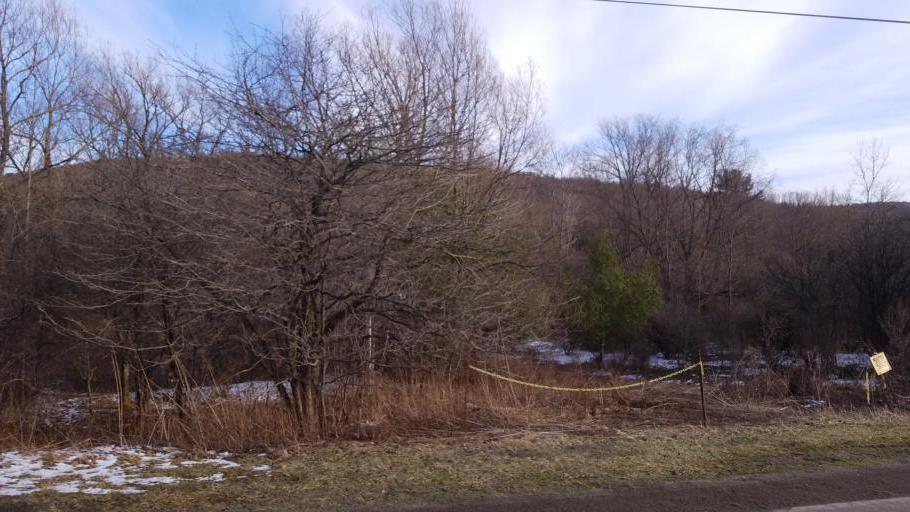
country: US
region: New York
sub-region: Allegany County
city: Wellsville
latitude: 42.1849
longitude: -77.9077
